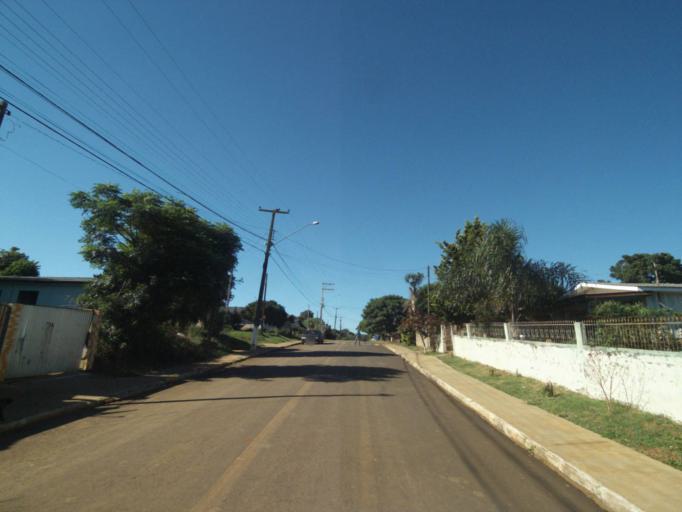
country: BR
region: Parana
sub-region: Pinhao
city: Pinhao
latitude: -25.8420
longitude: -52.0317
